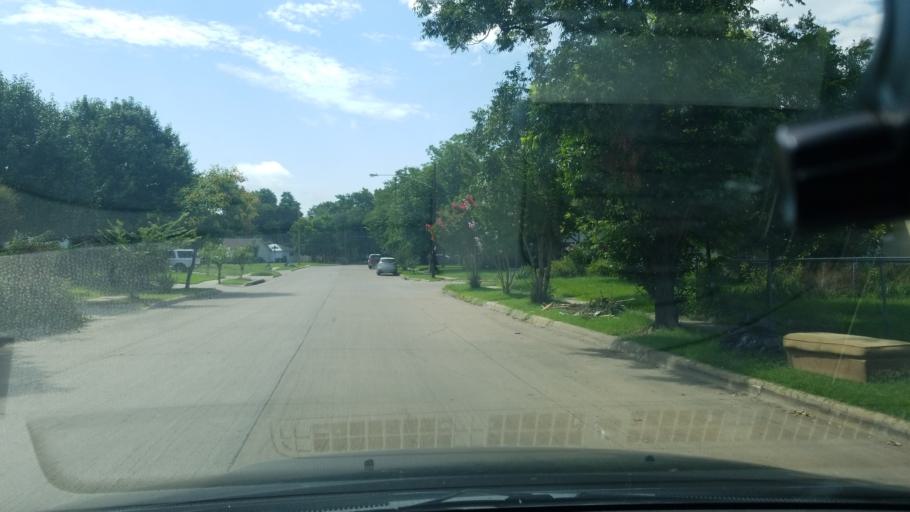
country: US
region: Texas
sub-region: Dallas County
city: Balch Springs
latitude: 32.7377
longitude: -96.6893
